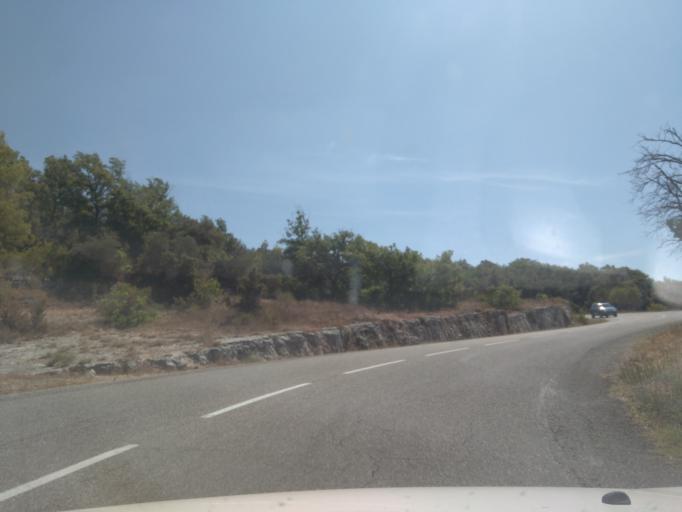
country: FR
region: Provence-Alpes-Cote d'Azur
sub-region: Departement du Var
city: Regusse
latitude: 43.7106
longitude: 6.0438
